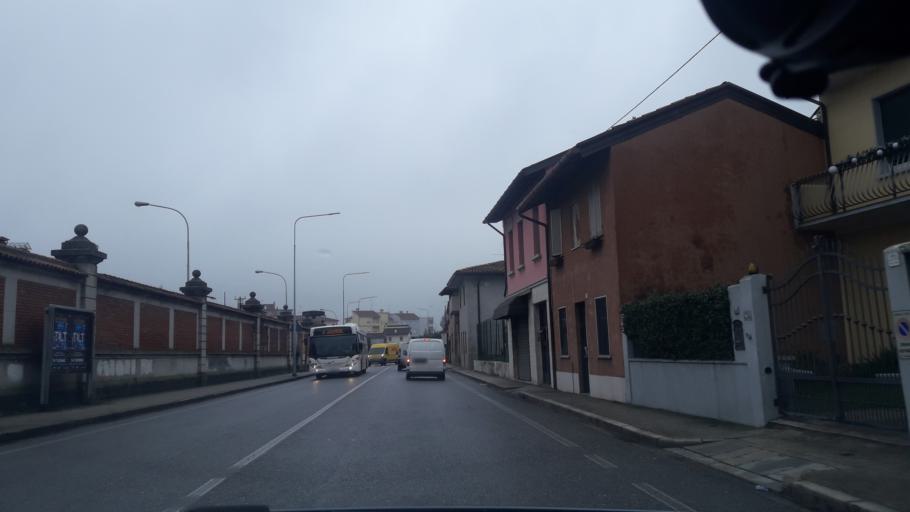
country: IT
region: Friuli Venezia Giulia
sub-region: Provincia di Udine
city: Udine
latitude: 46.0719
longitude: 13.2556
